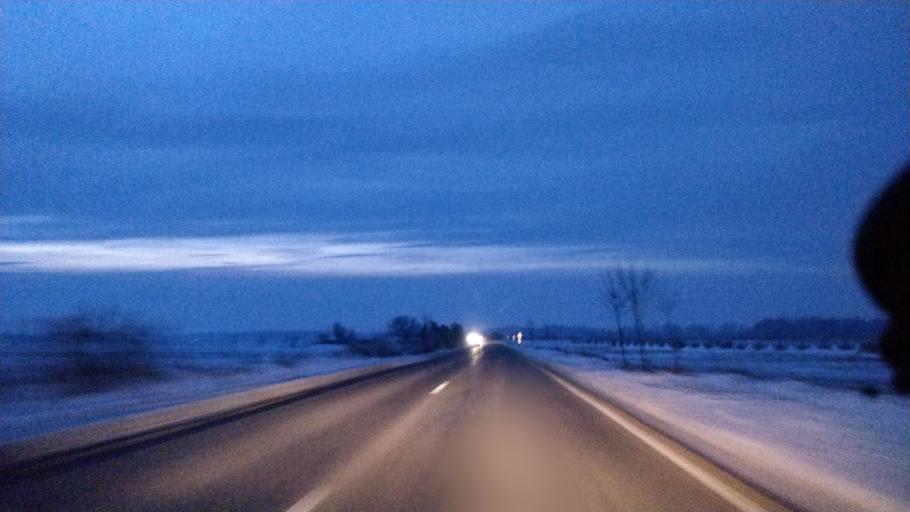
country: RO
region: Vrancea
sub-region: Comuna Suraia
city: Suraia
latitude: 45.6449
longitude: 27.3576
